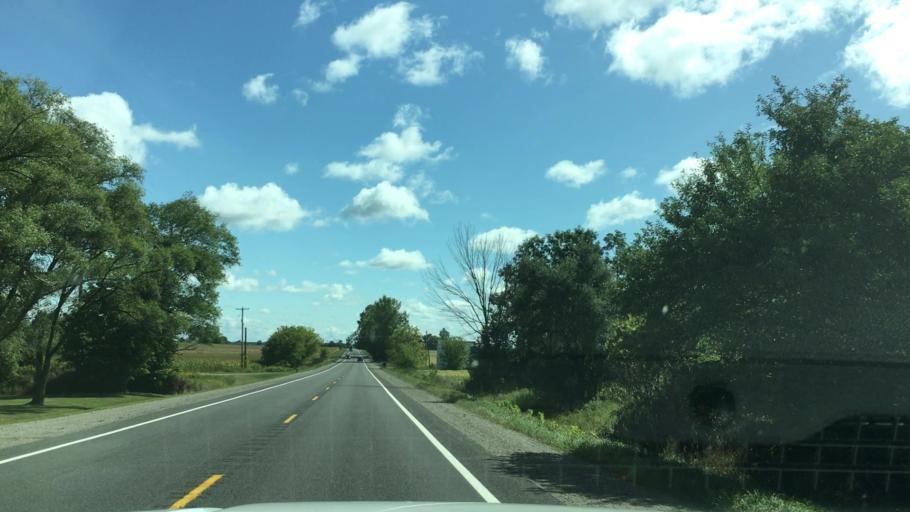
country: US
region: Michigan
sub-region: Montcalm County
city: Carson City
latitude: 43.1773
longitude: -84.9116
